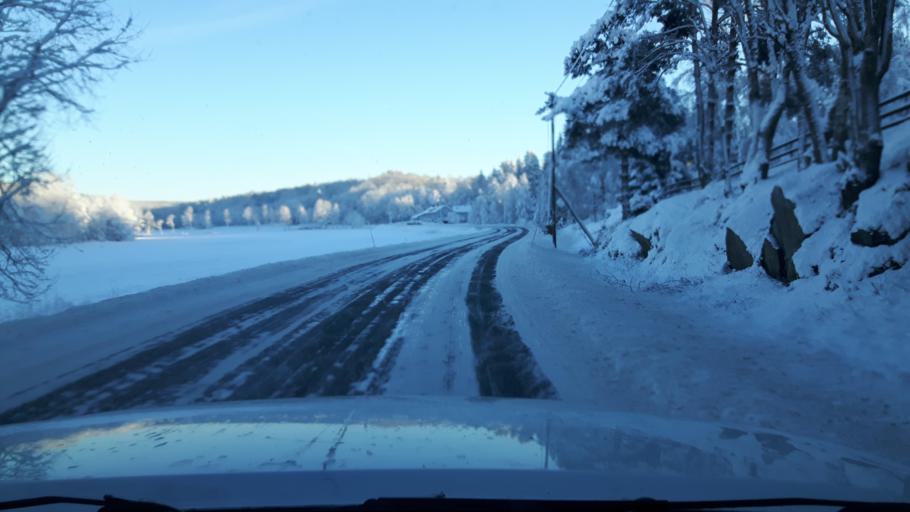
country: SE
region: Halland
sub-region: Kungsbacka Kommun
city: Fjaeras kyrkby
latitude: 57.5540
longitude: 12.2008
